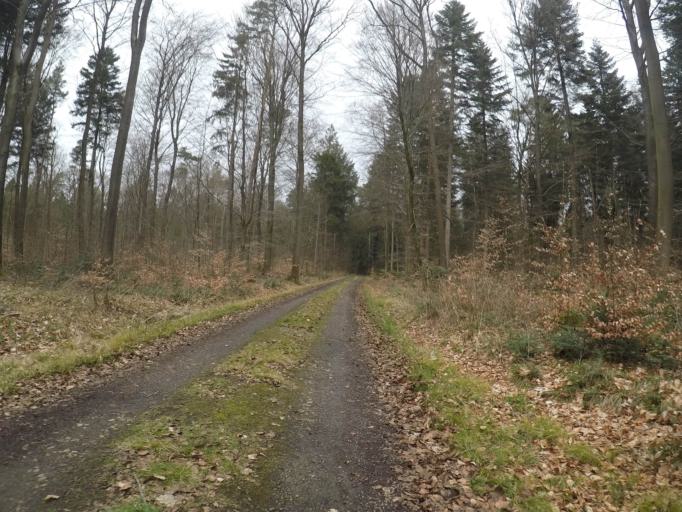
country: DE
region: Lower Saxony
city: Drangstedt
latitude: 53.6189
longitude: 8.7192
